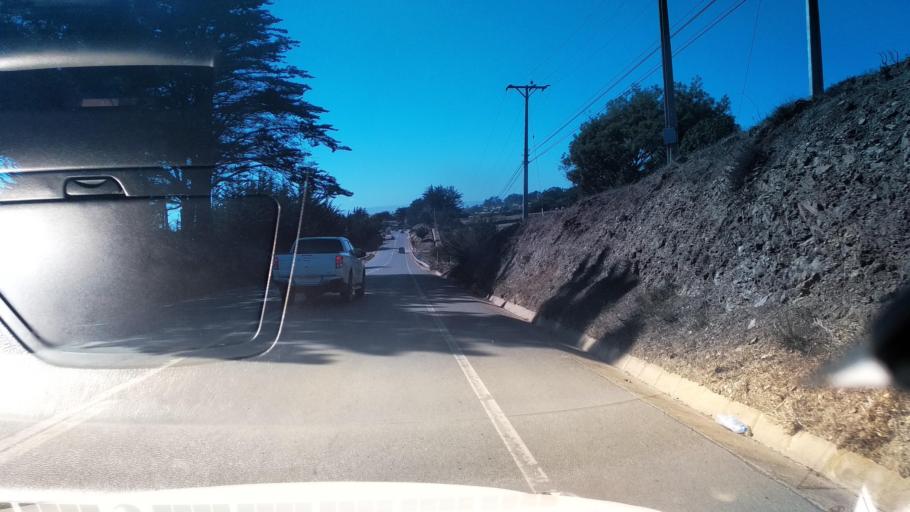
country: CL
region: O'Higgins
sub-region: Provincia de Colchagua
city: Santa Cruz
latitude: -34.4205
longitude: -72.0307
